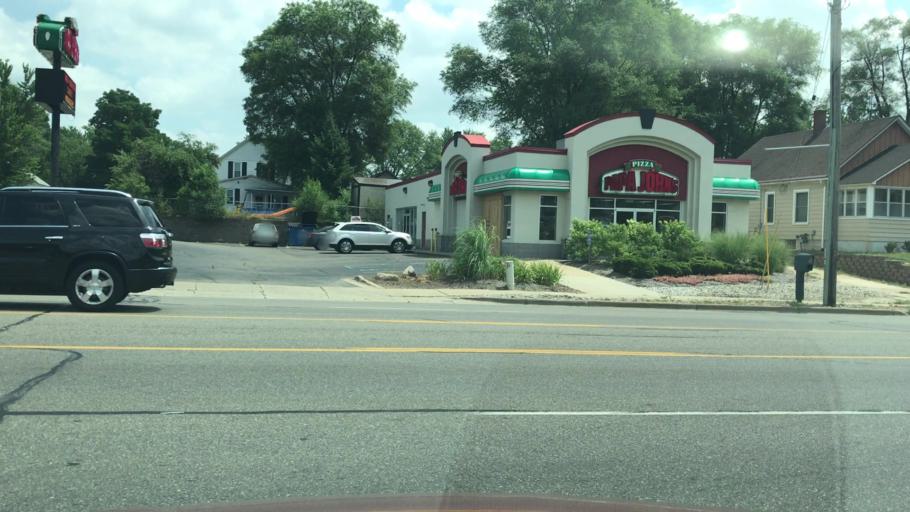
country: US
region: Michigan
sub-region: Kent County
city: Comstock Park
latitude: 43.0086
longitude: -85.6888
